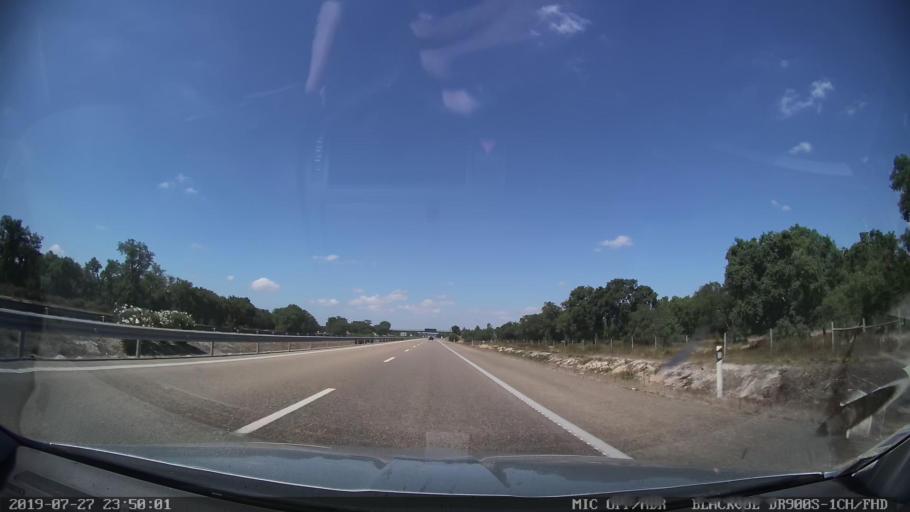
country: PT
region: Evora
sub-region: Vendas Novas
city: Vendas Novas
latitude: 38.6172
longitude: -8.5983
